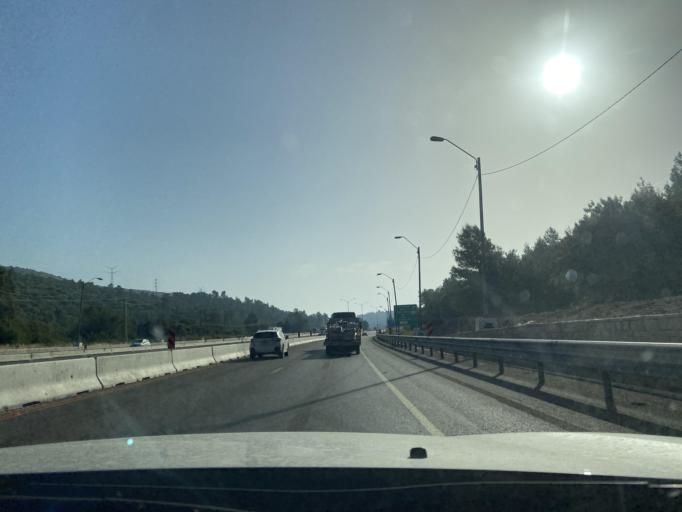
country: IL
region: Haifa
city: Daliyat el Karmil
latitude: 32.6503
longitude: 35.0862
